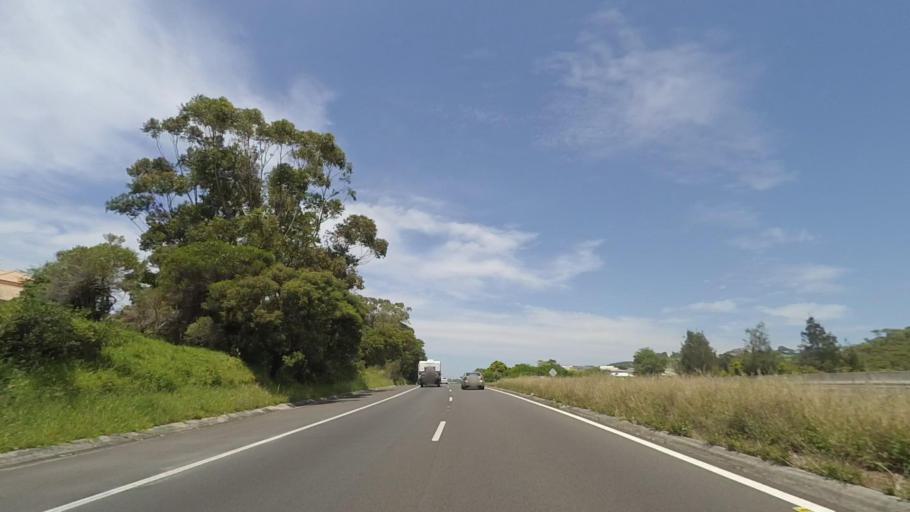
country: AU
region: New South Wales
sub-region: Kiama
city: Kiama
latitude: -34.6736
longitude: 150.8428
